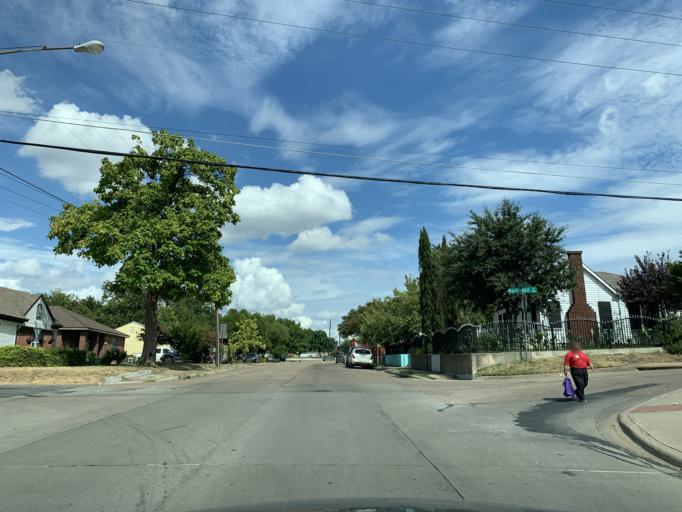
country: US
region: Texas
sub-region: Dallas County
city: Cockrell Hill
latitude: 32.7349
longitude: -96.8763
